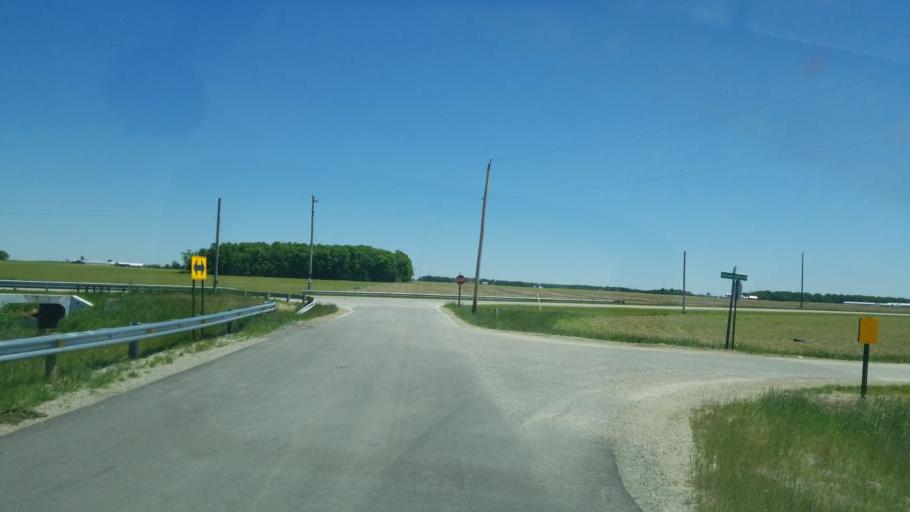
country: US
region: Ohio
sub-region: Darke County
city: Ansonia
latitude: 40.2795
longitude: -84.7097
